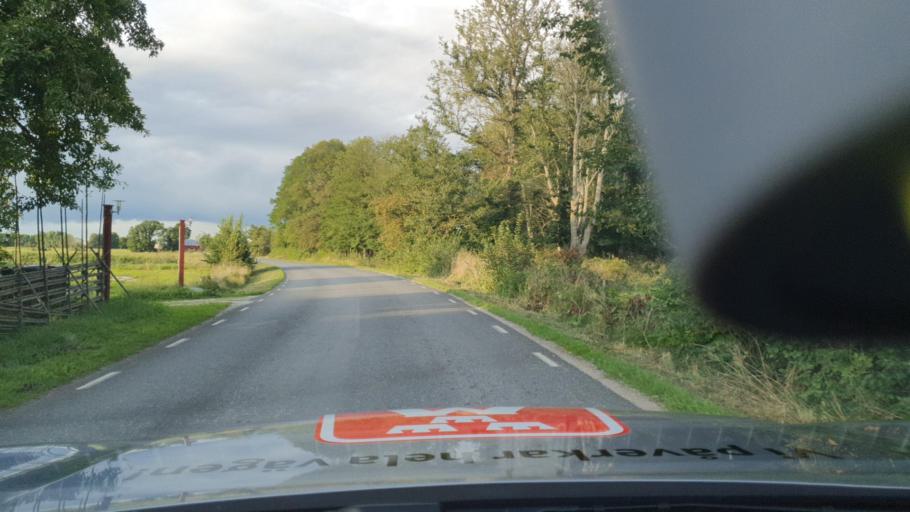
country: SE
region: Gotland
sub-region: Gotland
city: Vibble
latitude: 57.5162
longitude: 18.3371
